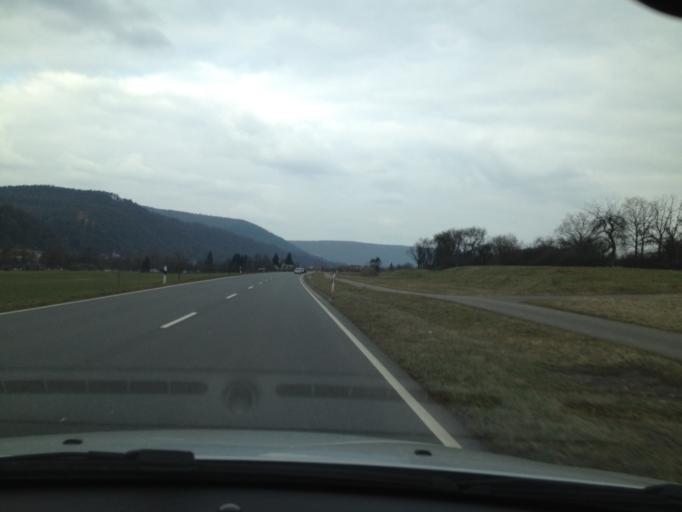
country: DE
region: Bavaria
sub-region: Regierungsbezirk Unterfranken
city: Stadtprozelten
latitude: 49.7757
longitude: 9.4074
